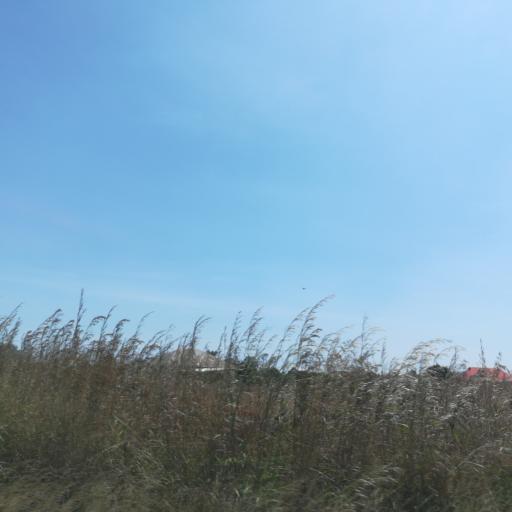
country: NG
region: Plateau
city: Bukuru
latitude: 9.7805
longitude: 8.9054
